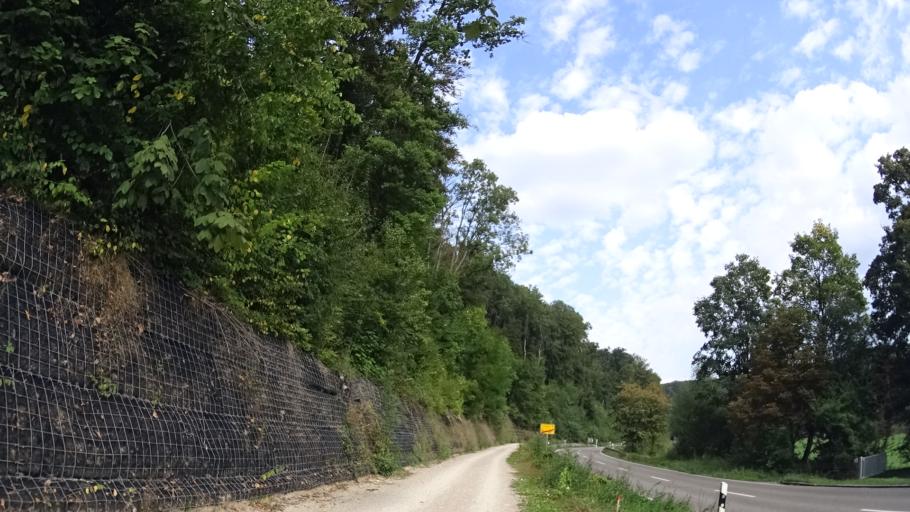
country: DE
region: Bavaria
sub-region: Lower Bavaria
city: Riedenburg
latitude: 48.9247
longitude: 11.6851
